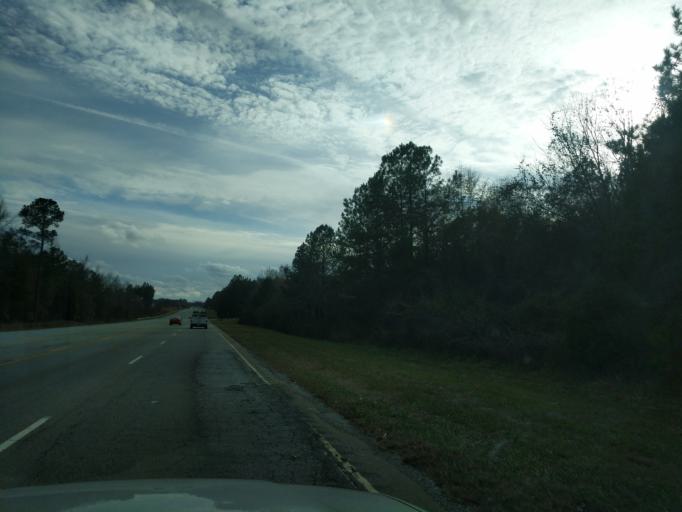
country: US
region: South Carolina
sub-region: Anderson County
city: Honea Path
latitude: 34.5450
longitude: -82.3167
